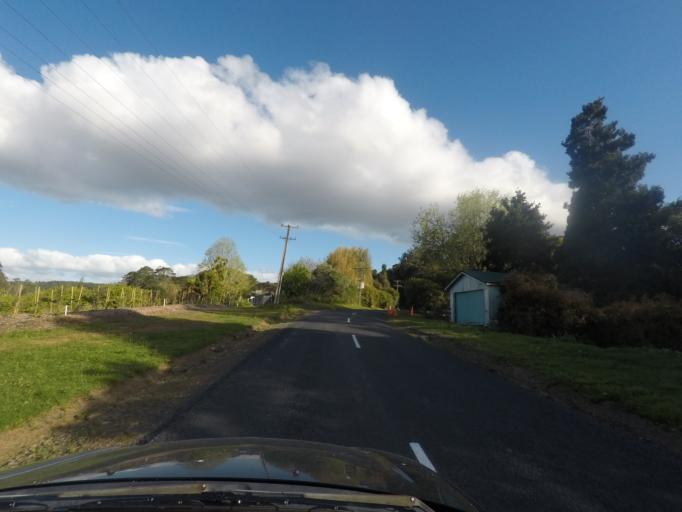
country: NZ
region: Auckland
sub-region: Auckland
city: Titirangi
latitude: -36.9246
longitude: 174.6187
